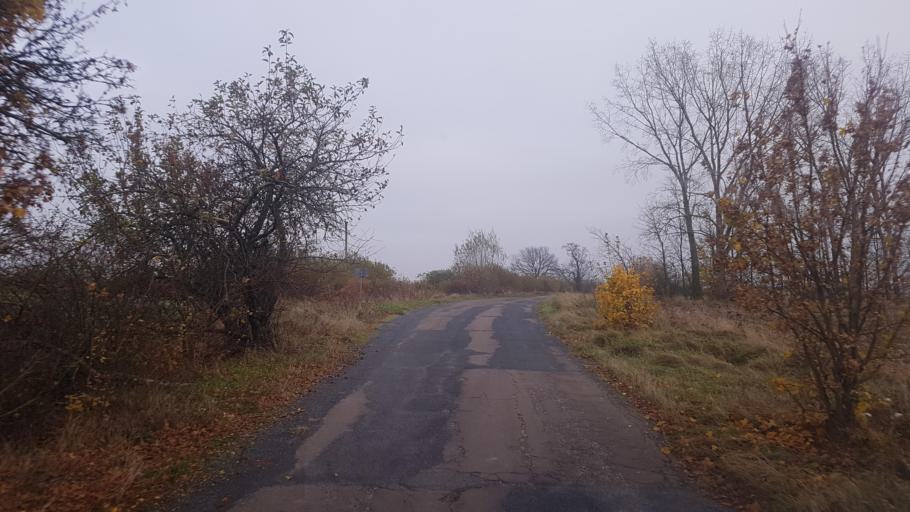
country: DE
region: Brandenburg
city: Gross Kreutz
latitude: 52.3685
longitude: 12.8214
